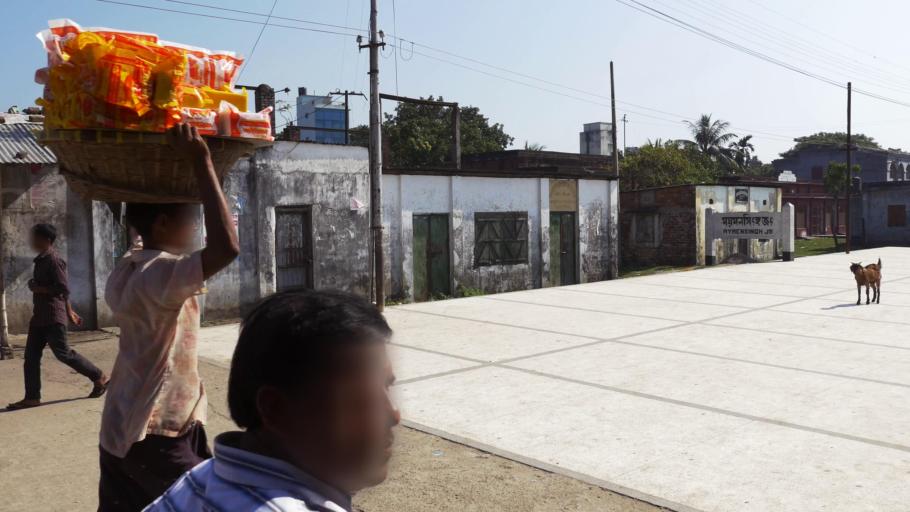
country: BD
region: Dhaka
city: Mymensingh
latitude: 24.6412
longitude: 90.4549
